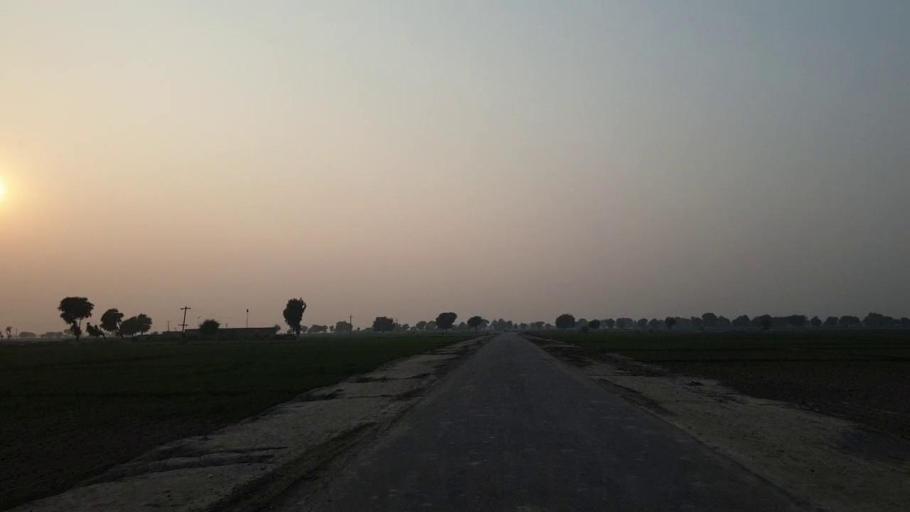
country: PK
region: Sindh
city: Bhan
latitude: 26.5305
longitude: 67.6995
